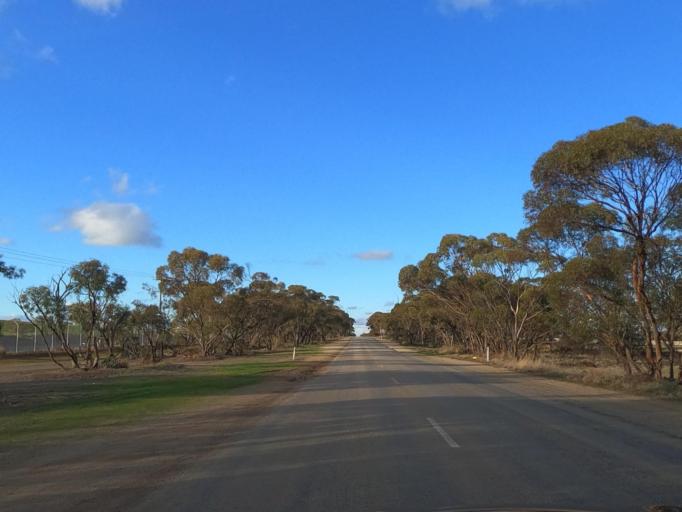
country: AU
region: Victoria
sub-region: Swan Hill
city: Swan Hill
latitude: -35.3501
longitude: 143.5105
